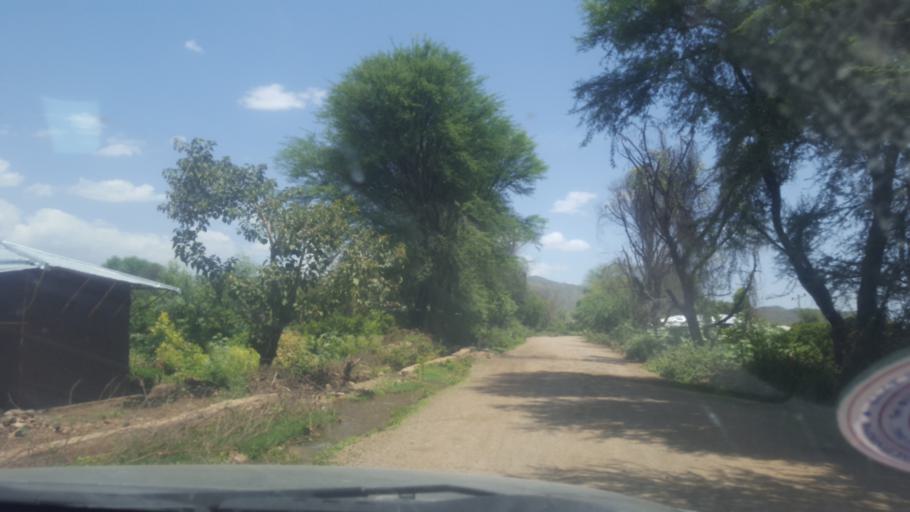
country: ET
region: Oromiya
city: Deder
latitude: 9.5326
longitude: 41.4165
